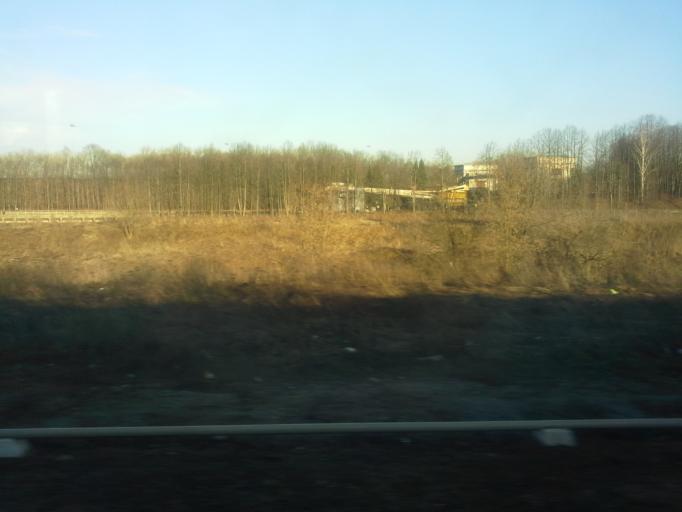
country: RU
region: Moskovskaya
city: Iksha
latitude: 56.1705
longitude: 37.5085
